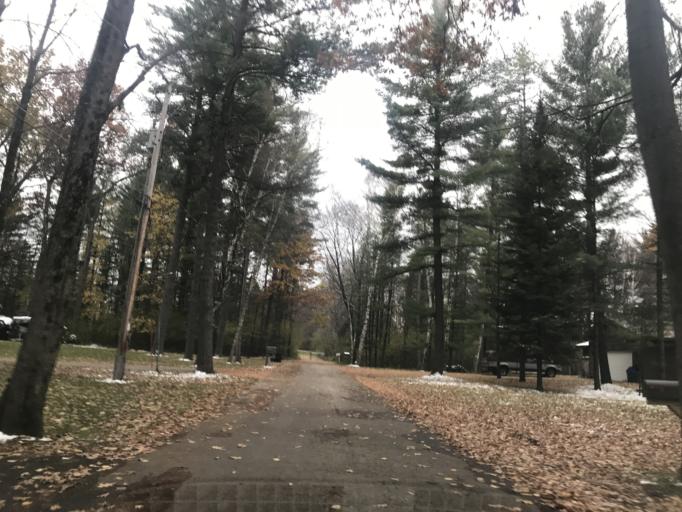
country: US
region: Wisconsin
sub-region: Marinette County
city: Marinette
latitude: 45.0960
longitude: -87.6557
